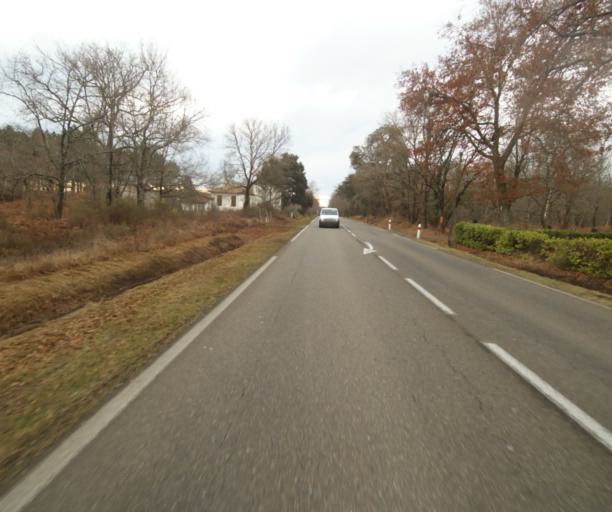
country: FR
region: Aquitaine
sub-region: Departement des Landes
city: Gabarret
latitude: 44.1001
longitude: -0.0162
